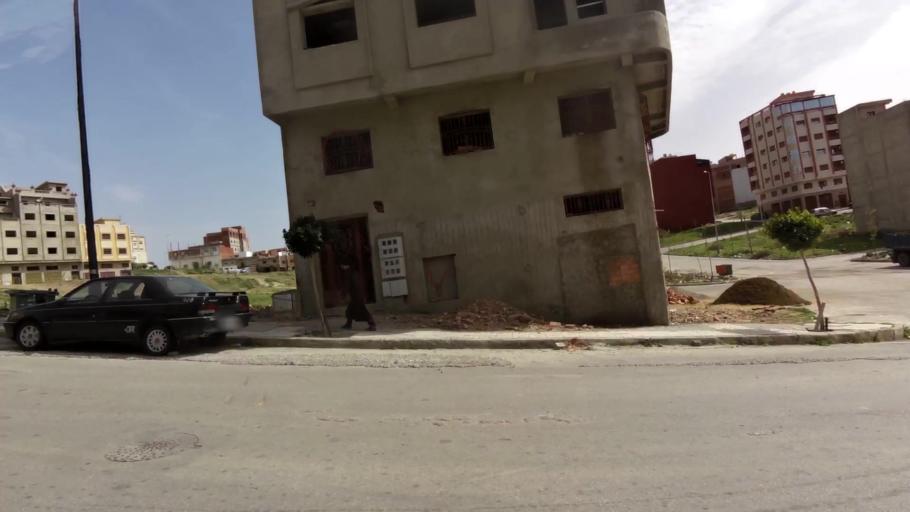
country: MA
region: Tanger-Tetouan
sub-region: Tanger-Assilah
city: Tangier
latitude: 35.7385
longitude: -5.8354
